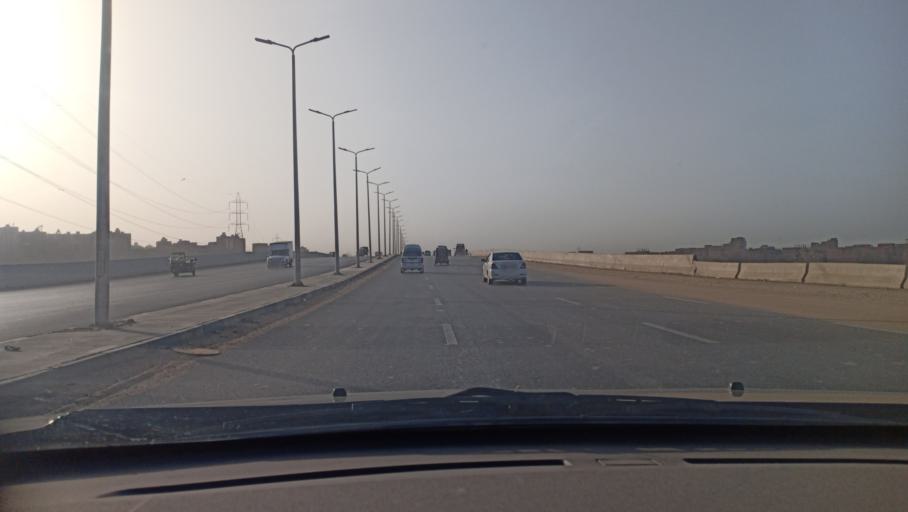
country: EG
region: Muhafazat al Qalyubiyah
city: Qalyub
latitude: 30.1420
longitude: 31.2633
